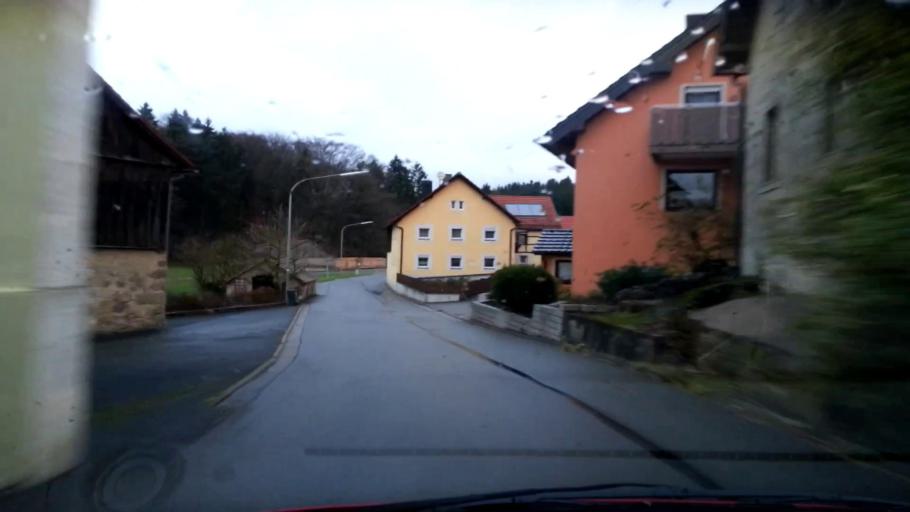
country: DE
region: Bavaria
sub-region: Upper Franconia
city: Aufsess
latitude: 49.9305
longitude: 11.2045
